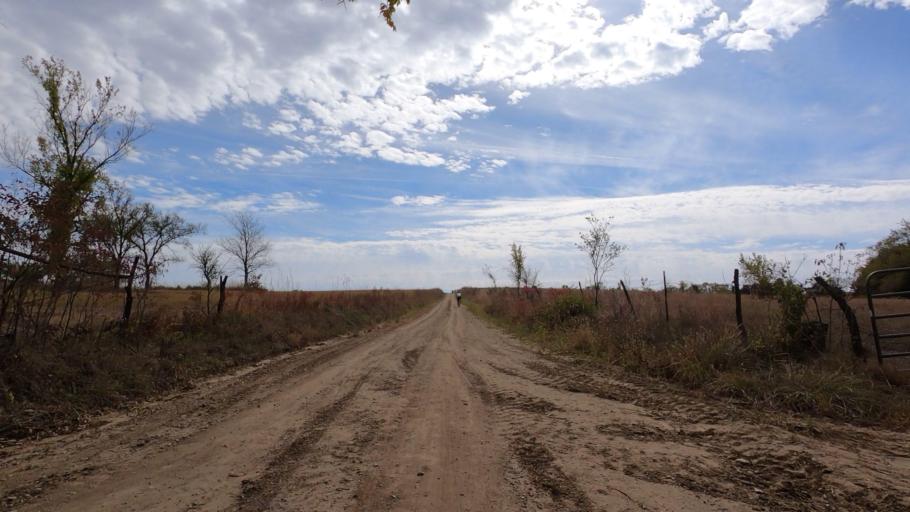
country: US
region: Kansas
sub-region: Pottawatomie County
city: Westmoreland
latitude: 39.3270
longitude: -96.4454
